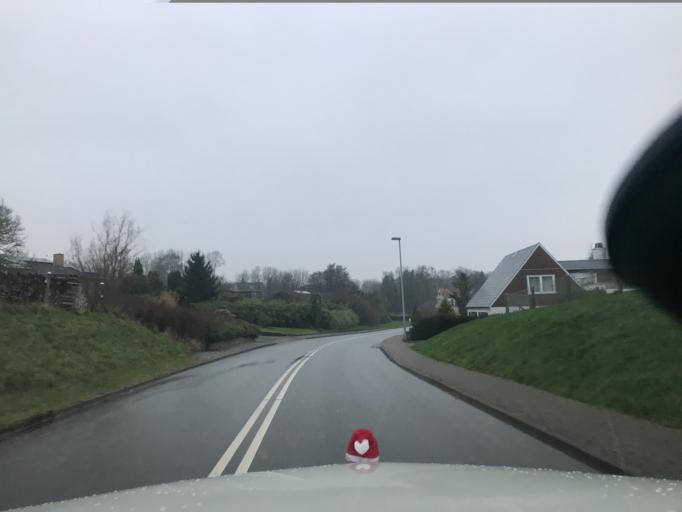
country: DK
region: South Denmark
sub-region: Sonderborg Kommune
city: Grasten
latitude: 54.9003
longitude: 9.5695
